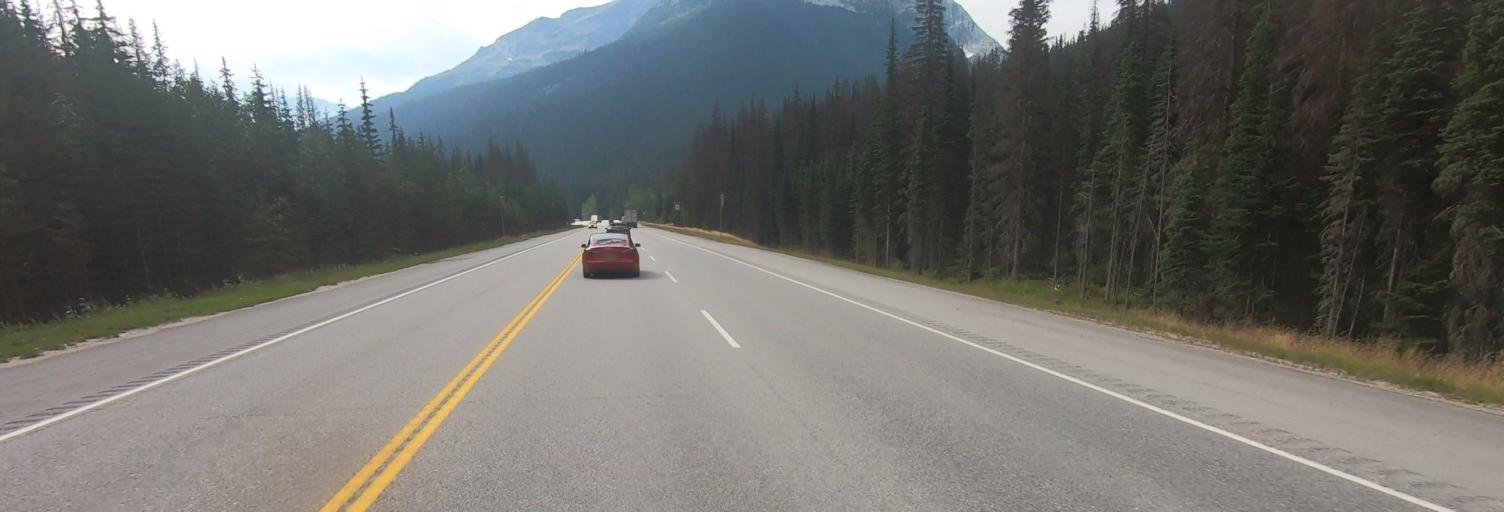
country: CA
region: British Columbia
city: Golden
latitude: 51.3091
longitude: -117.5174
